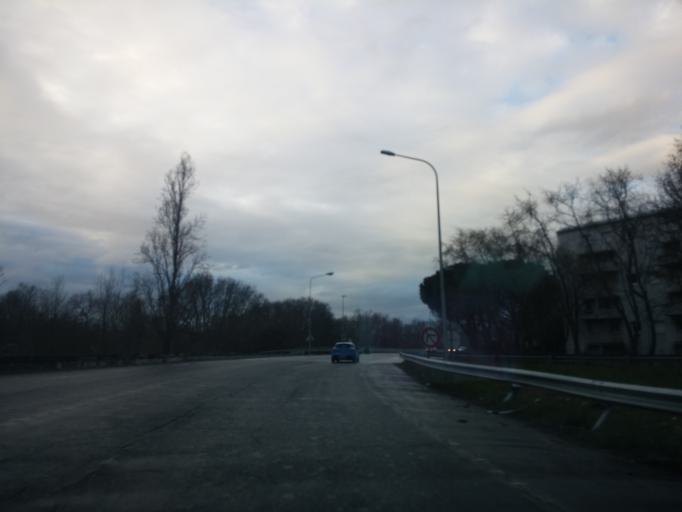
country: FR
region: Midi-Pyrenees
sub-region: Departement de la Haute-Garonne
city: Toulouse
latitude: 43.5751
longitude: 1.4365
